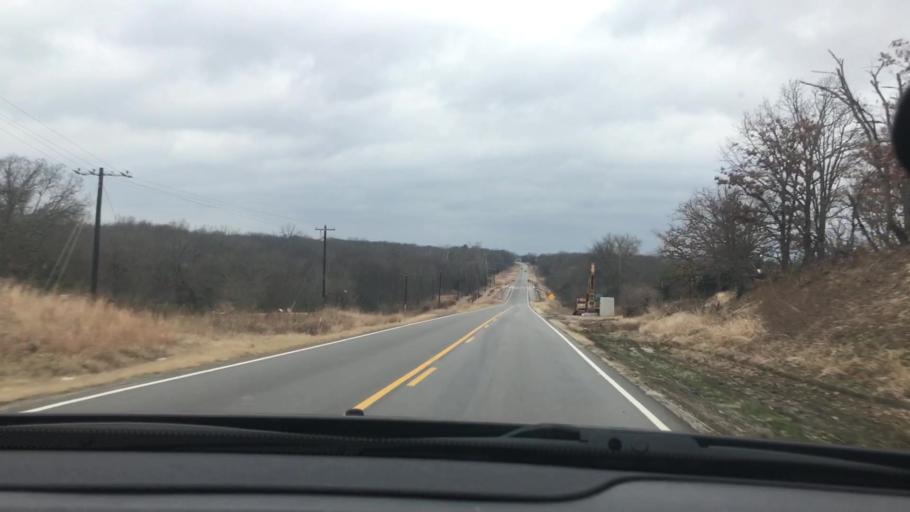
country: US
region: Oklahoma
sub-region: Atoka County
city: Atoka
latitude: 34.3791
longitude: -96.2744
